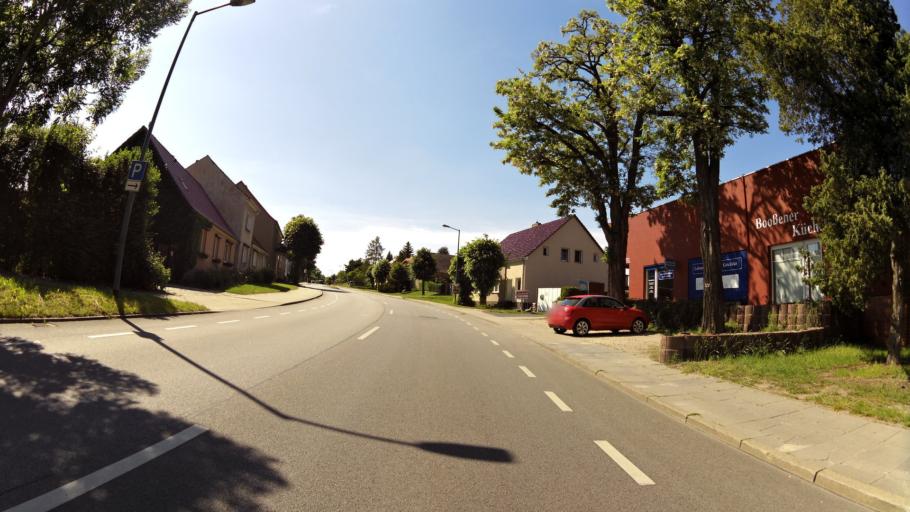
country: DE
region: Brandenburg
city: Frankfurt (Oder)
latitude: 52.3712
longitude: 14.4805
